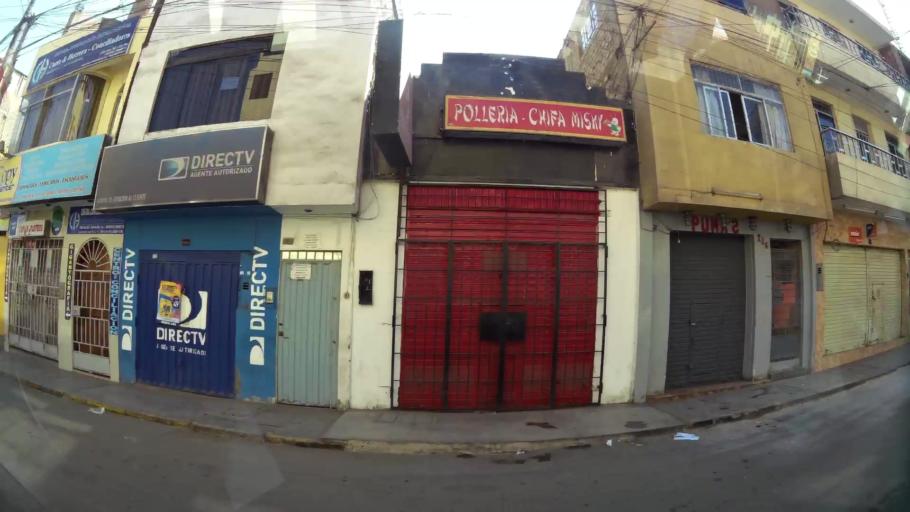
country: PE
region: Ica
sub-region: Provincia de Chincha
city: Chincha Alta
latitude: -13.4189
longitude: -76.1325
